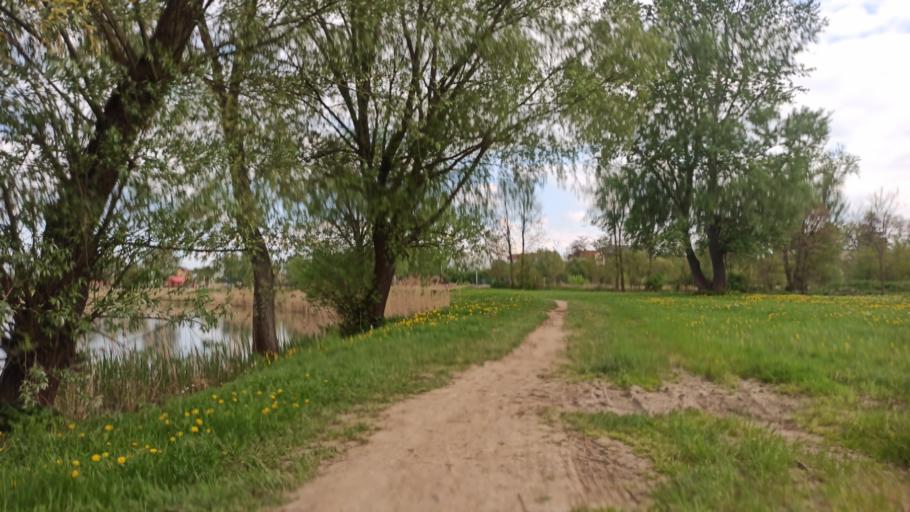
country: PL
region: Subcarpathian Voivodeship
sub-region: Powiat jaroslawski
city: Radymno
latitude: 49.9515
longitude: 22.8252
